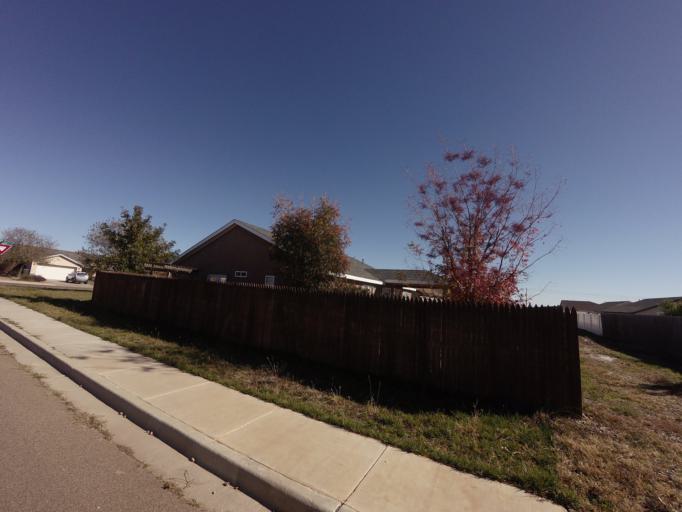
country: US
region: New Mexico
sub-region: Curry County
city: Clovis
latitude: 34.4152
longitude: -103.1623
